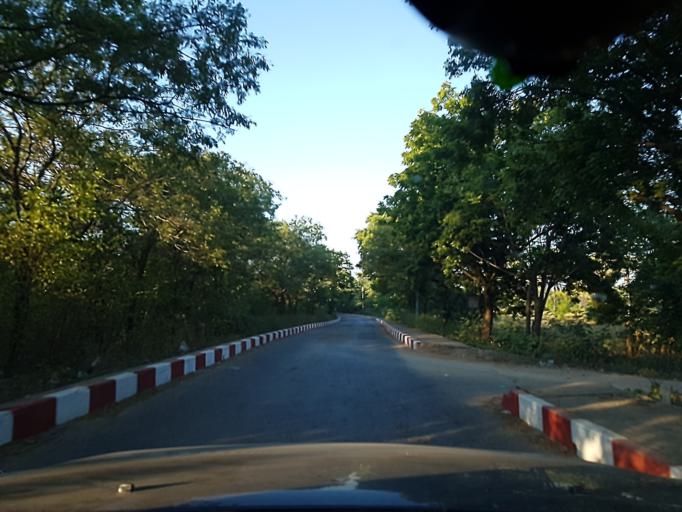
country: MM
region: Sagain
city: Monywa
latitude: 21.8013
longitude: 95.1669
